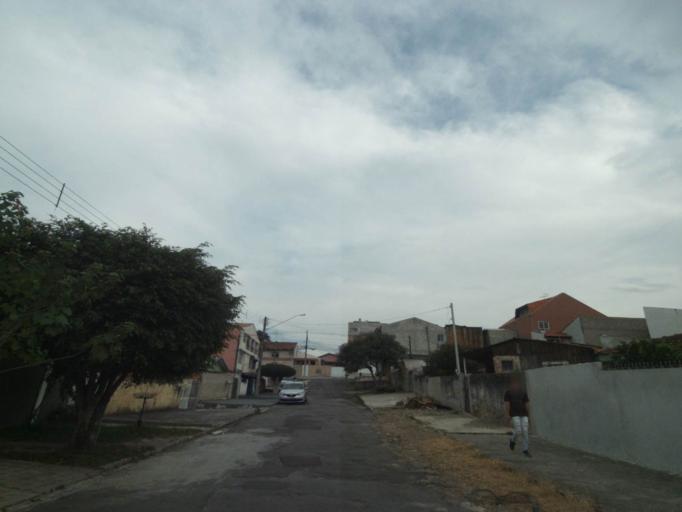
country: BR
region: Parana
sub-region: Pinhais
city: Pinhais
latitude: -25.4491
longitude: -49.2217
